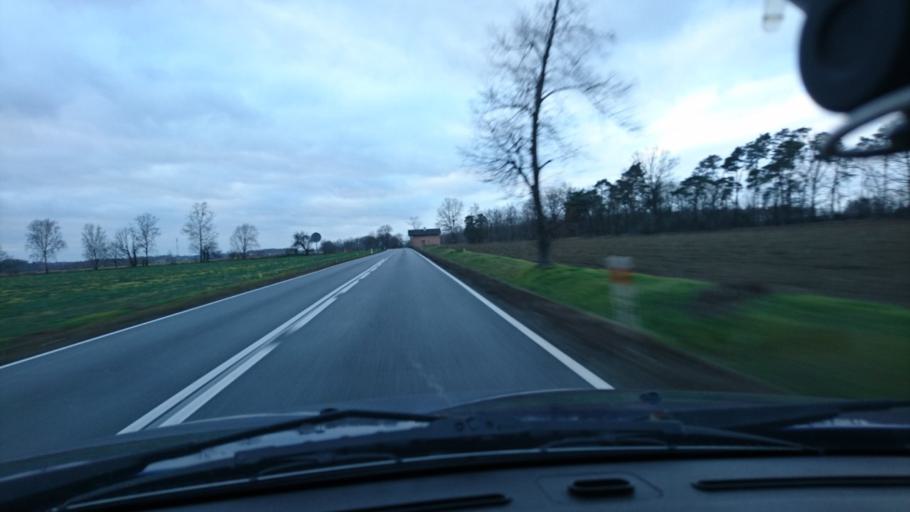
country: PL
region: Lodz Voivodeship
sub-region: Powiat wieruszowski
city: Boleslawiec
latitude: 51.1519
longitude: 18.1818
